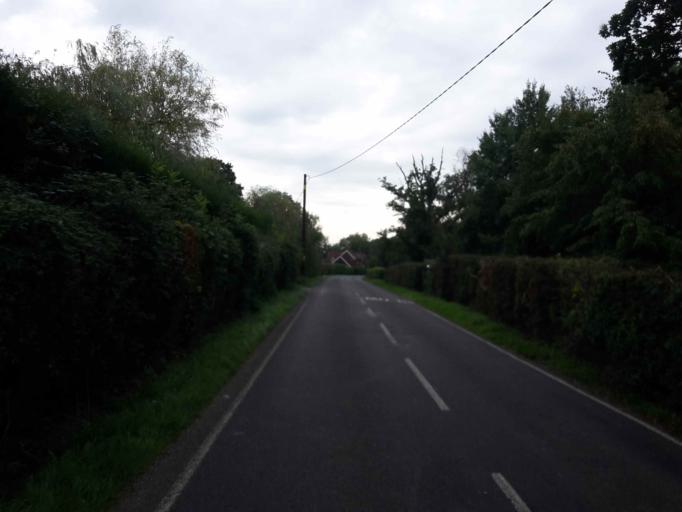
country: GB
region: England
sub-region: West Sussex
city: Rudgwick
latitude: 51.0641
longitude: -0.4467
